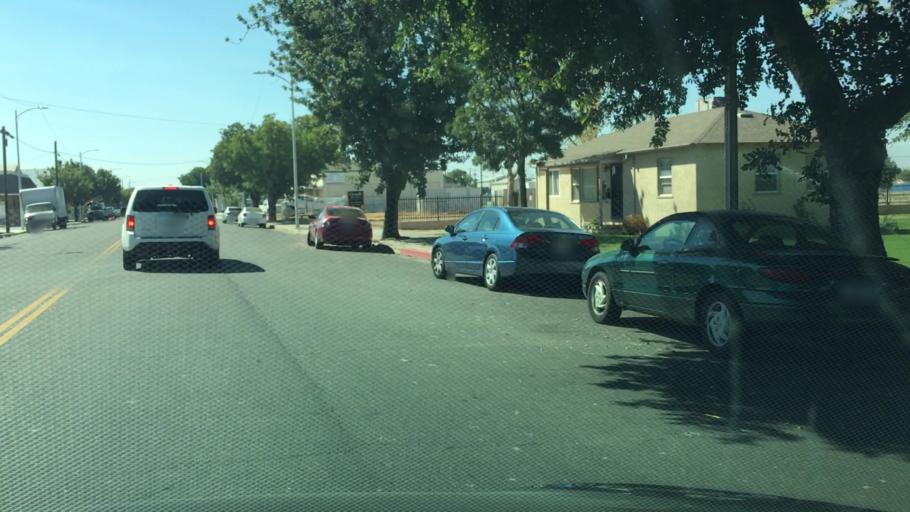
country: US
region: California
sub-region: Merced County
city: Los Banos
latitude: 37.0577
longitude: -120.8407
